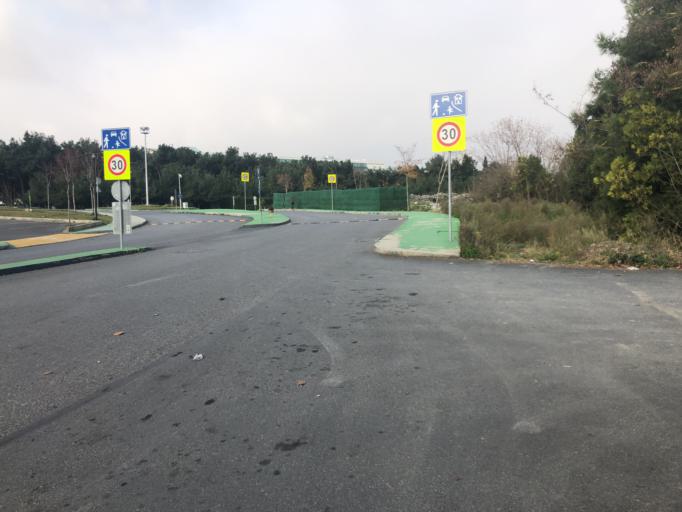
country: TR
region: Istanbul
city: merter keresteciler
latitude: 41.0194
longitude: 28.8930
